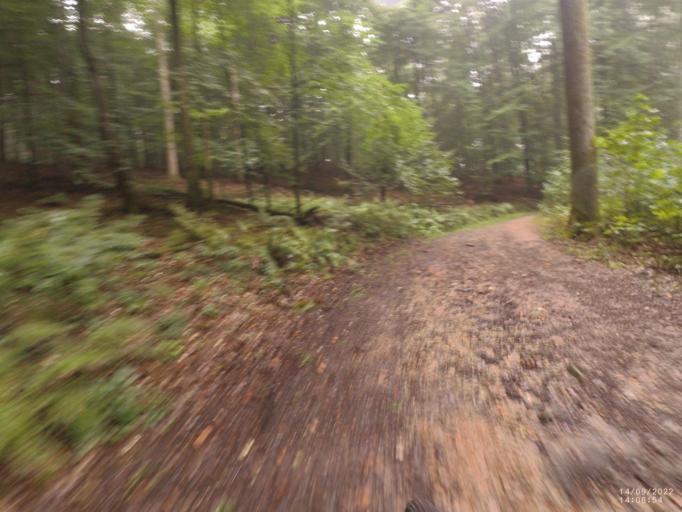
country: DE
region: Bavaria
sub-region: Regierungsbezirk Unterfranken
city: Johannesberg
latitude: 50.0189
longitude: 9.1444
